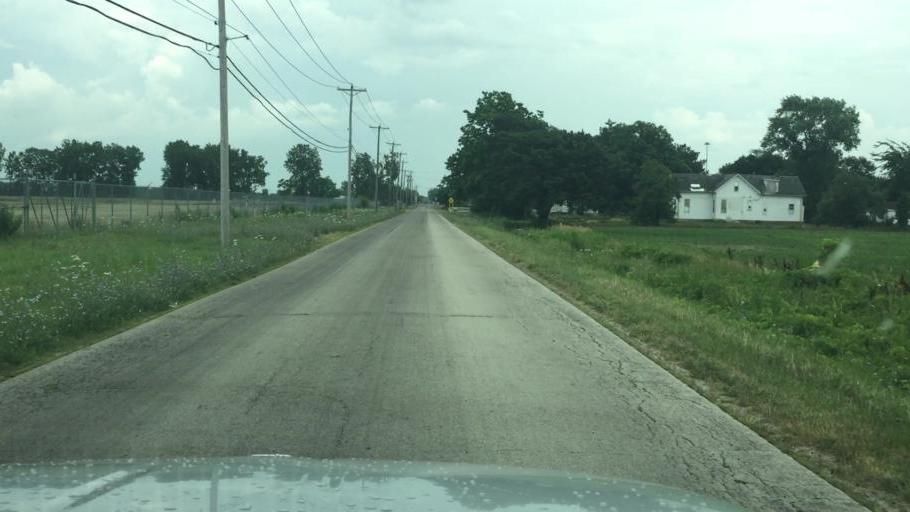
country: US
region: Ohio
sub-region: Wood County
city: Walbridge
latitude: 41.5879
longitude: -83.5215
